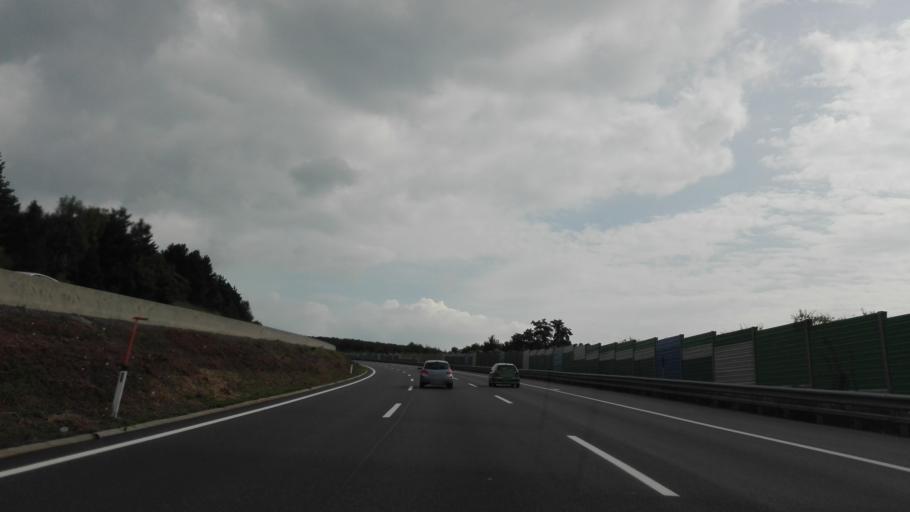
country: AT
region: Lower Austria
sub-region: Politischer Bezirk Modling
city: Giesshubl
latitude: 48.0861
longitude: 16.2312
